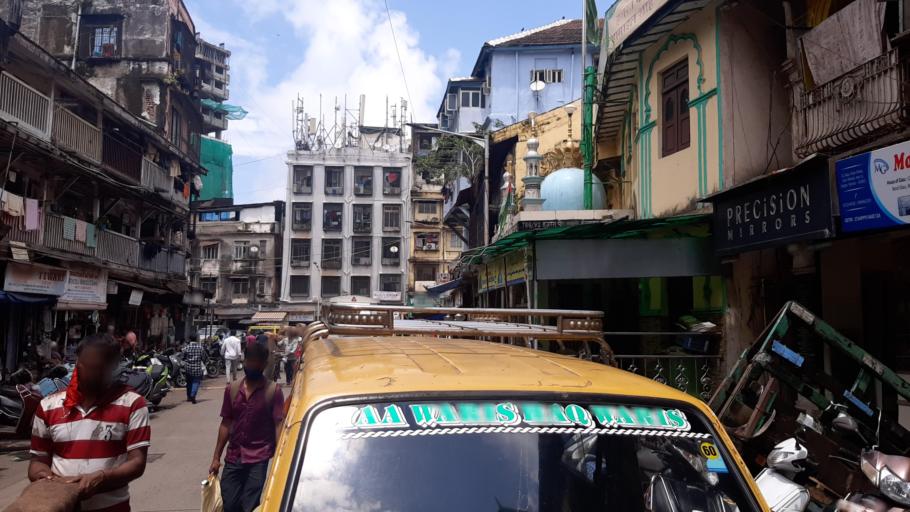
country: IN
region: Maharashtra
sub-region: Mumbai Suburban
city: Mumbai
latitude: 18.9565
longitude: 72.8292
